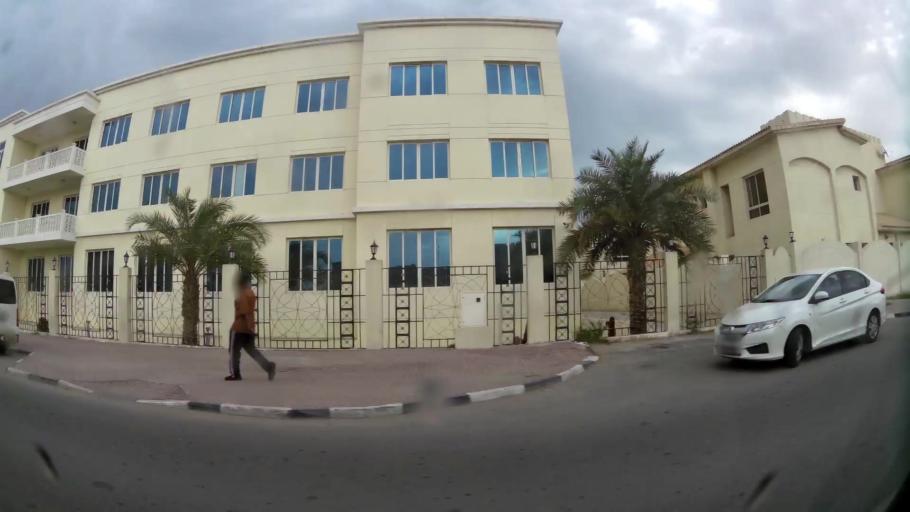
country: QA
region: Baladiyat ad Dawhah
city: Doha
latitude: 25.2710
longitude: 51.4998
